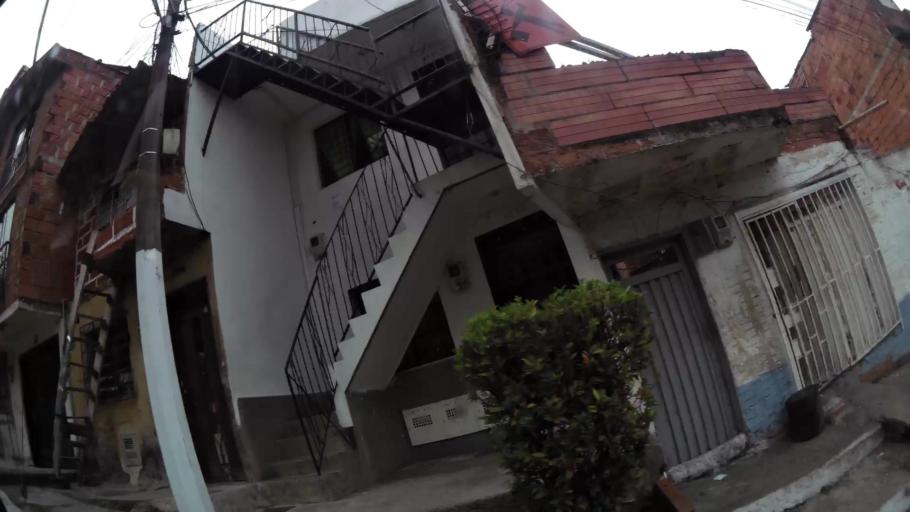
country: CO
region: Antioquia
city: Medellin
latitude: 6.2892
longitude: -75.5550
